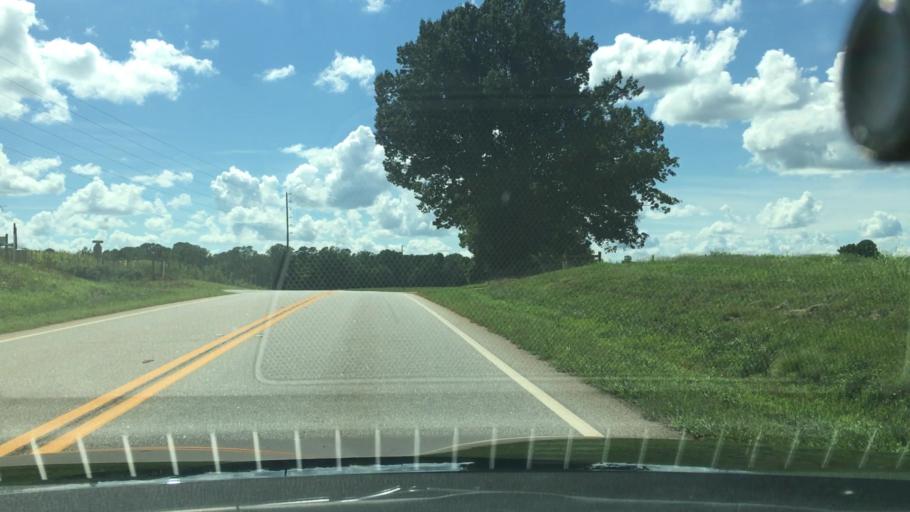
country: US
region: Georgia
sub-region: Jasper County
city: Monticello
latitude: 33.3004
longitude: -83.7208
